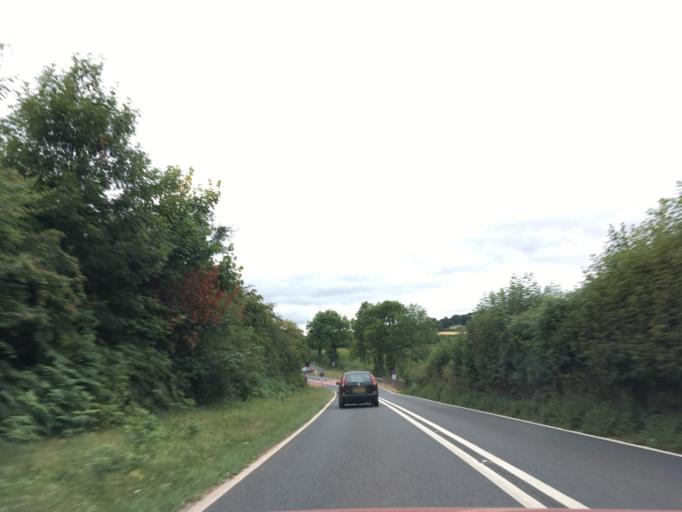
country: GB
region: Wales
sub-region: Blaenau Gwent
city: Brynmawr
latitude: 51.8943
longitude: -3.2462
